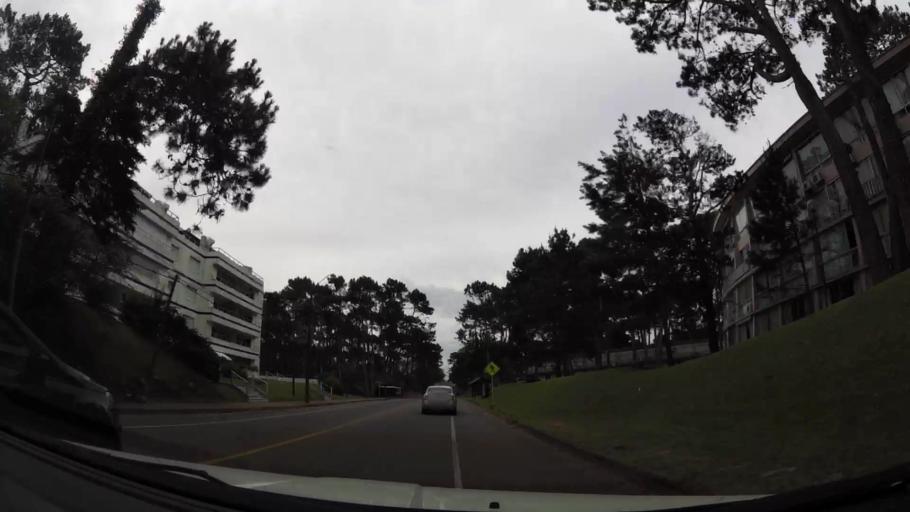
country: UY
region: Maldonado
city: Maldonado
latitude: -34.9266
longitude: -54.9561
